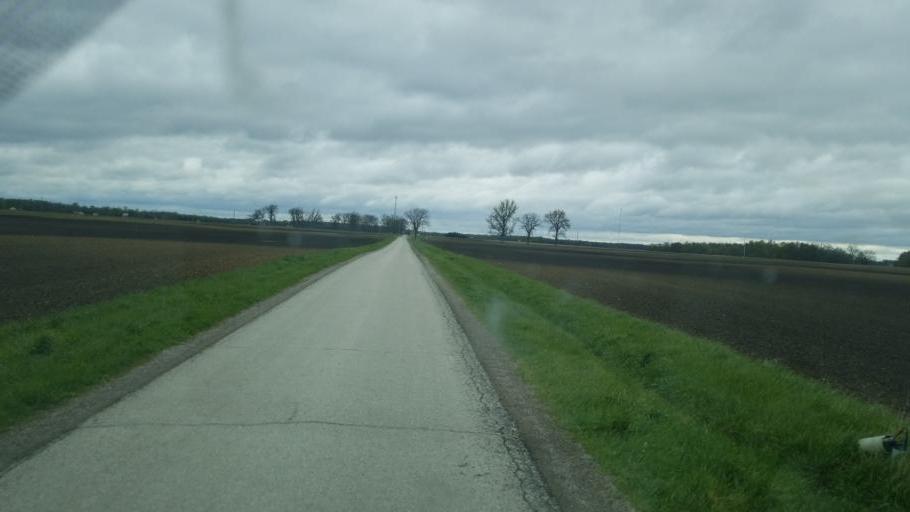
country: US
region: Ohio
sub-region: Crawford County
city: Bucyrus
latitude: 40.7286
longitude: -83.0734
